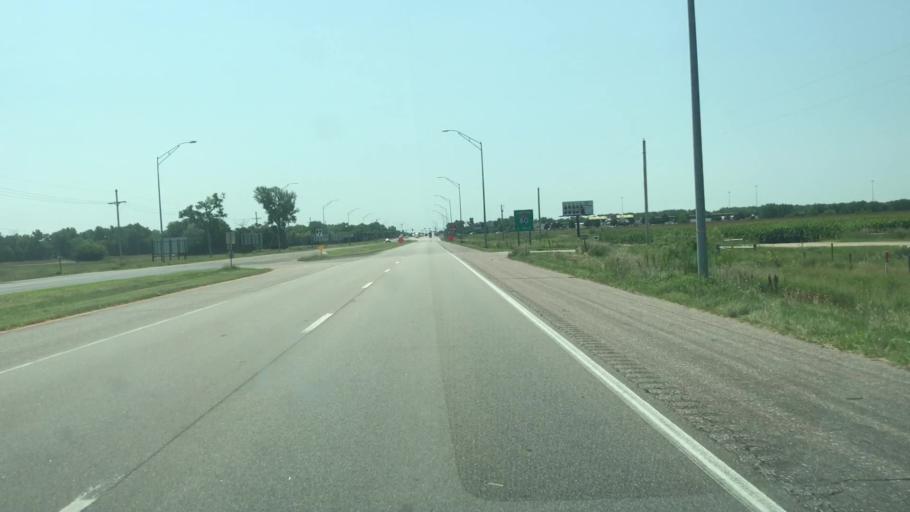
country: US
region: Nebraska
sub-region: Hall County
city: Grand Island
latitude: 40.8378
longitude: -98.3787
